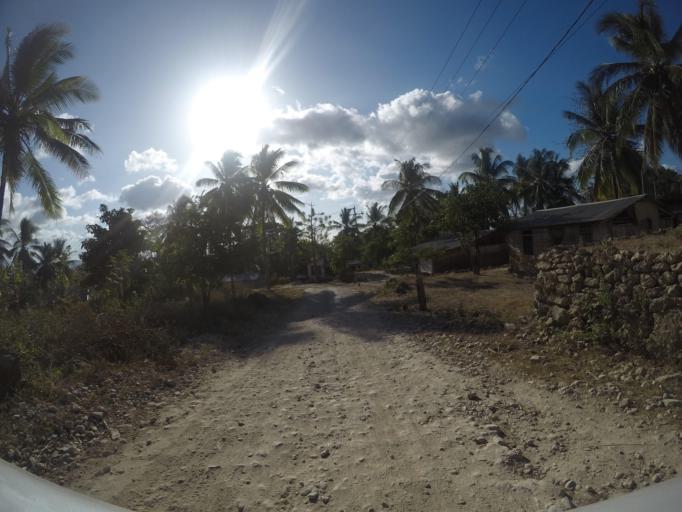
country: TL
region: Lautem
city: Lospalos
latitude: -8.4384
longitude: 126.8580
